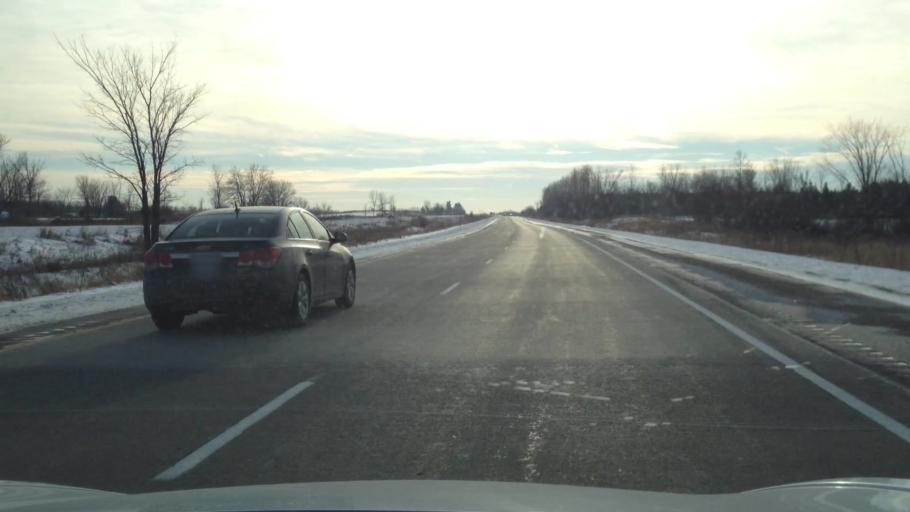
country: CA
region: Ontario
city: Hawkesbury
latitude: 45.5433
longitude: -74.5416
